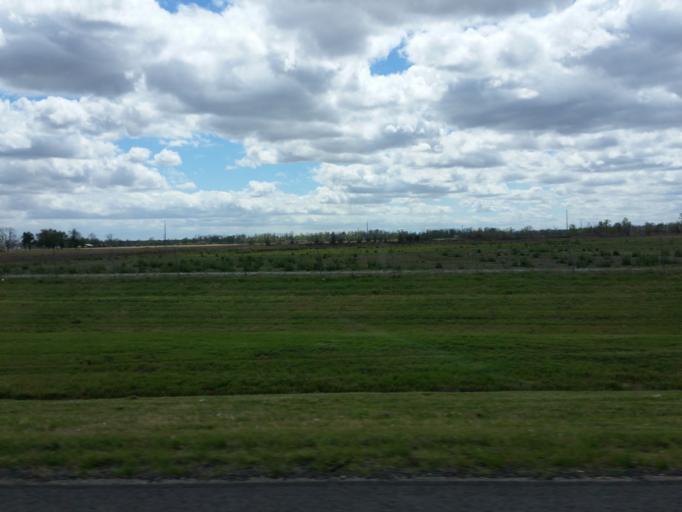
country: US
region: Arkansas
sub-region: Poinsett County
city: Marked Tree
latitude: 35.5276
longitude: -90.4360
